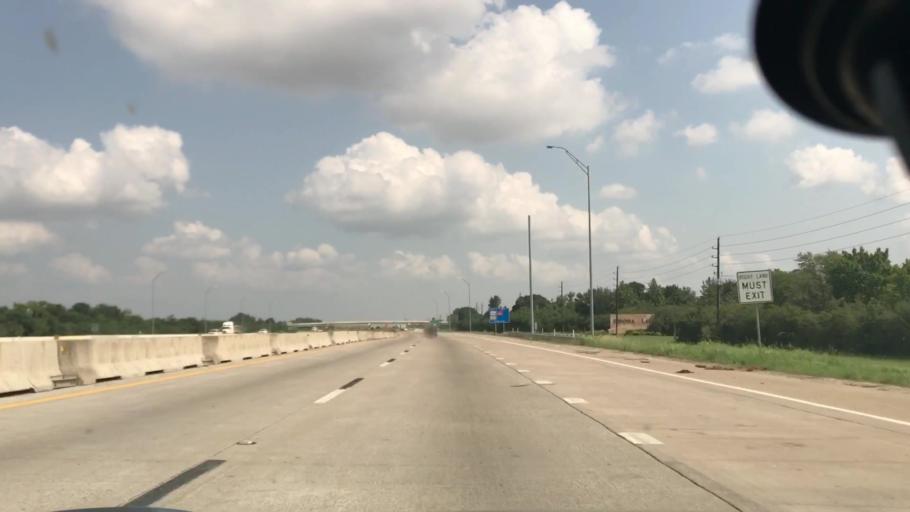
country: US
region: Texas
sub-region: Brazoria County
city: Iowa Colony
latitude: 29.5184
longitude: -95.3866
